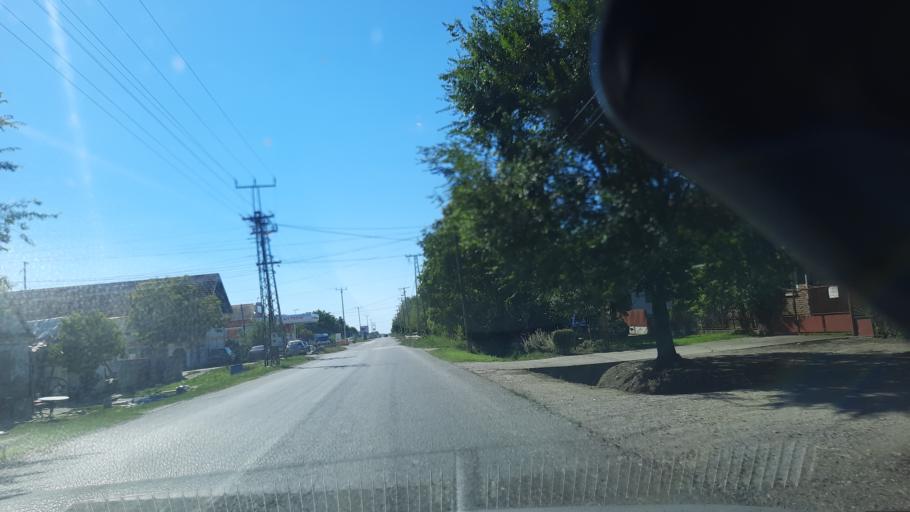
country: RS
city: Simanovci
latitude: 44.8763
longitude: 20.0773
